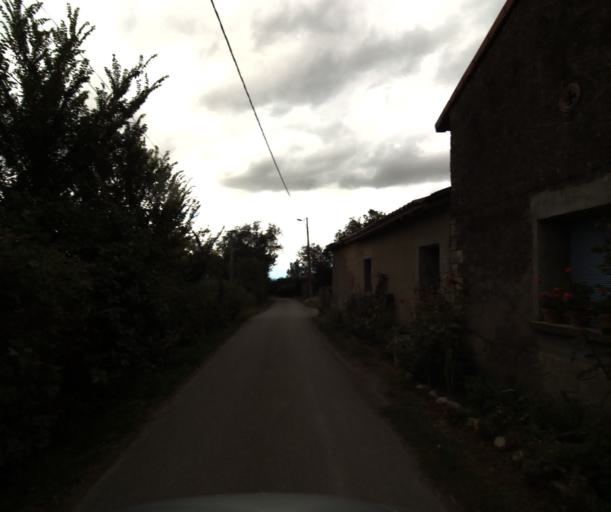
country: FR
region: Midi-Pyrenees
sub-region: Departement de la Haute-Garonne
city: Le Fauga
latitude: 43.4016
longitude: 1.3129
